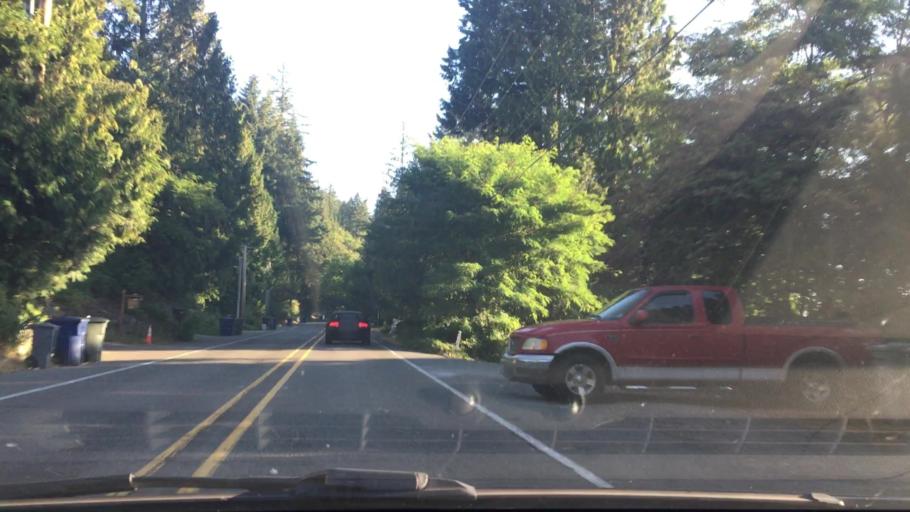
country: US
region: Washington
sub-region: King County
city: West Lake Sammamish
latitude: 47.5904
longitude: -122.1119
